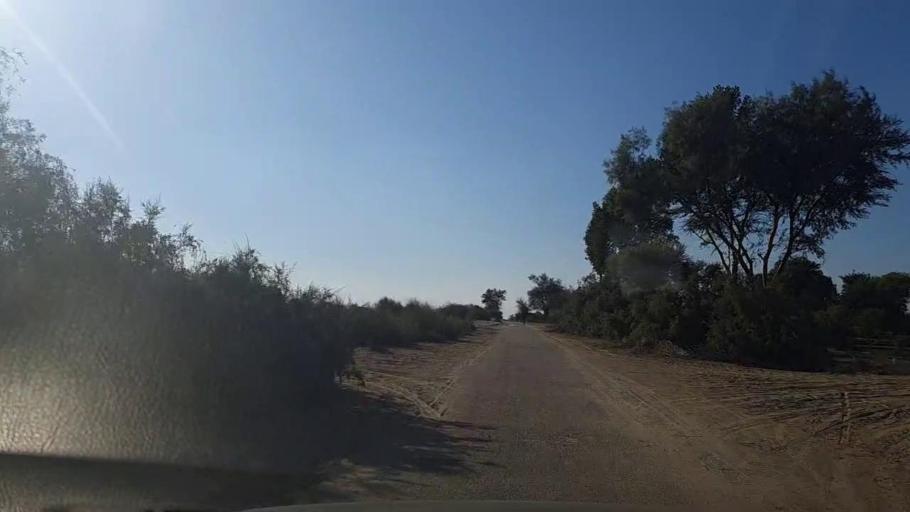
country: PK
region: Sindh
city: Khadro
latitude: 26.2412
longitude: 68.8902
